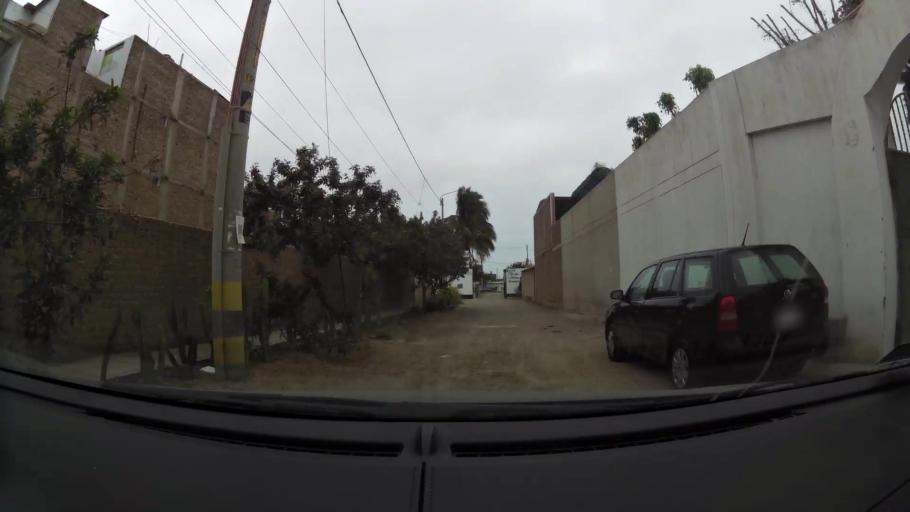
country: PE
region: La Libertad
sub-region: Provincia de Trujillo
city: Trujillo
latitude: -8.1210
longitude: -79.0444
